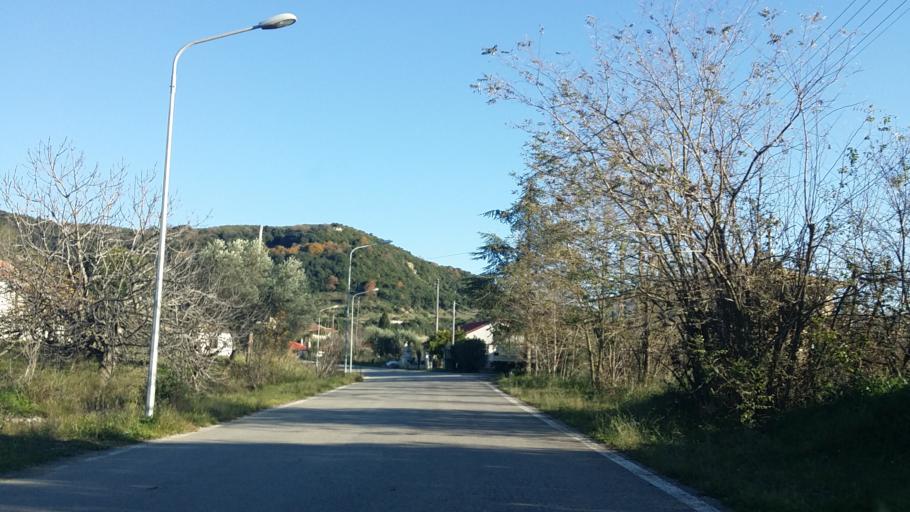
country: GR
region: West Greece
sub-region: Nomos Aitolias kai Akarnanias
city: Sardinia
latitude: 38.8737
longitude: 21.2552
